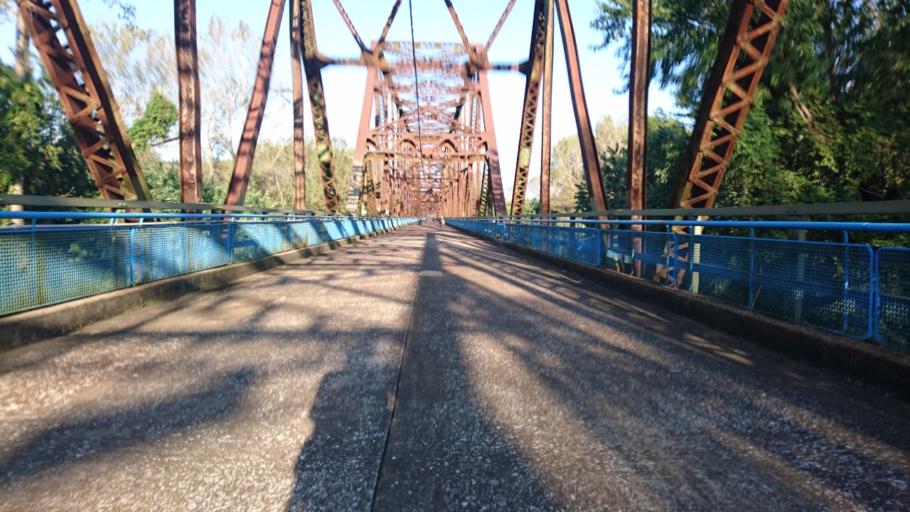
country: US
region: Missouri
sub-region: Saint Louis County
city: Glasgow Village
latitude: 38.7577
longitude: -90.1669
